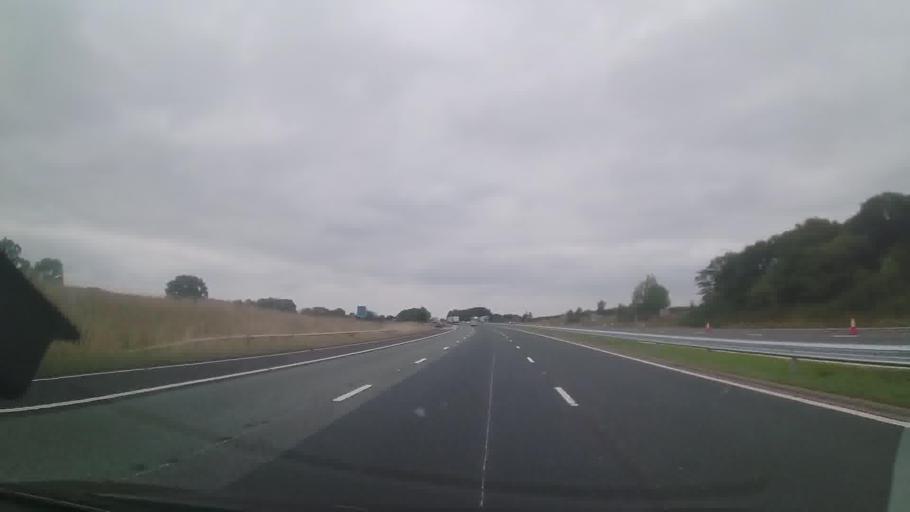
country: GB
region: England
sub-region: Cumbria
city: Scotby
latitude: 54.8000
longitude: -2.8722
